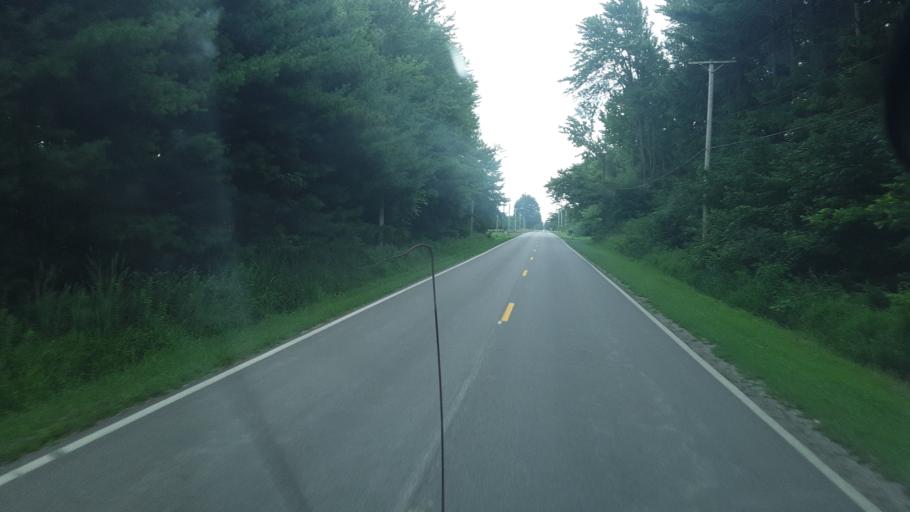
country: US
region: Ohio
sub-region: Ashtabula County
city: Jefferson
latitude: 41.6802
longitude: -80.7493
